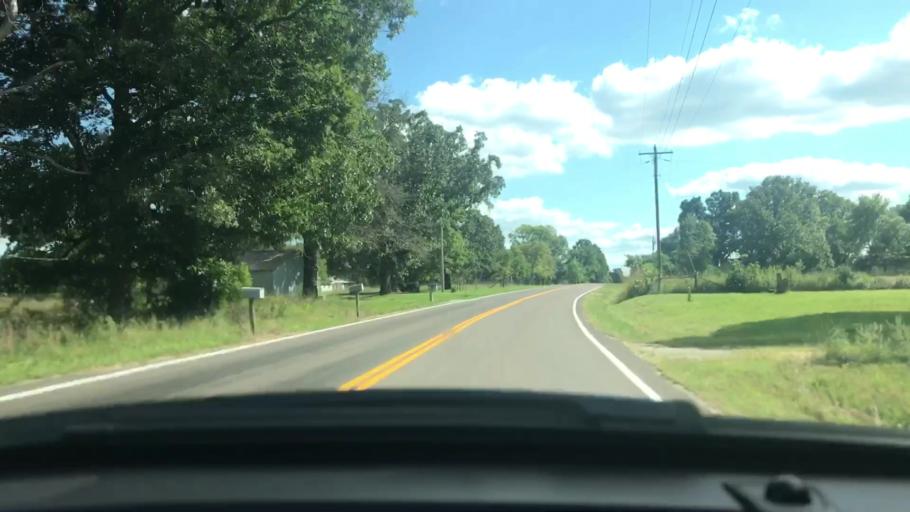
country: US
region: Missouri
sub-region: Wright County
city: Mountain Grove
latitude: 37.2277
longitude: -92.2929
